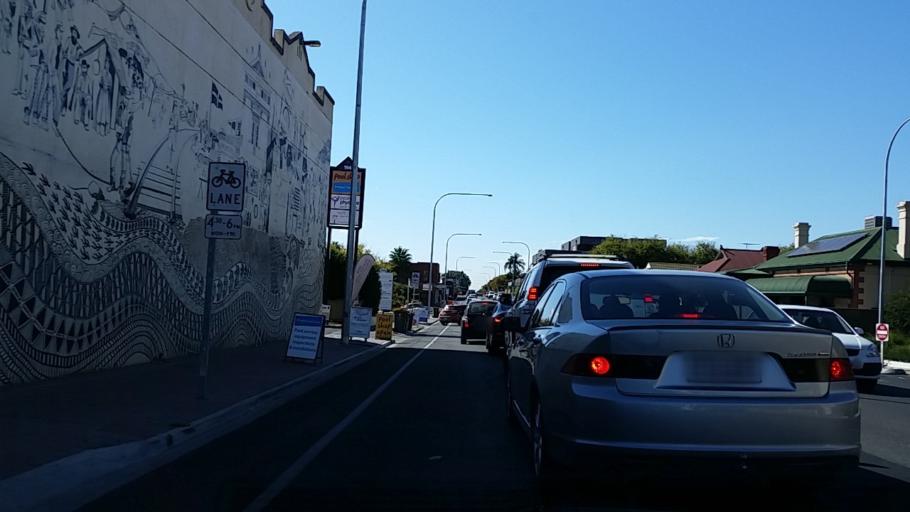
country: AU
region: South Australia
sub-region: Prospect
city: Prospect
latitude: -34.8812
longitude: 138.5936
